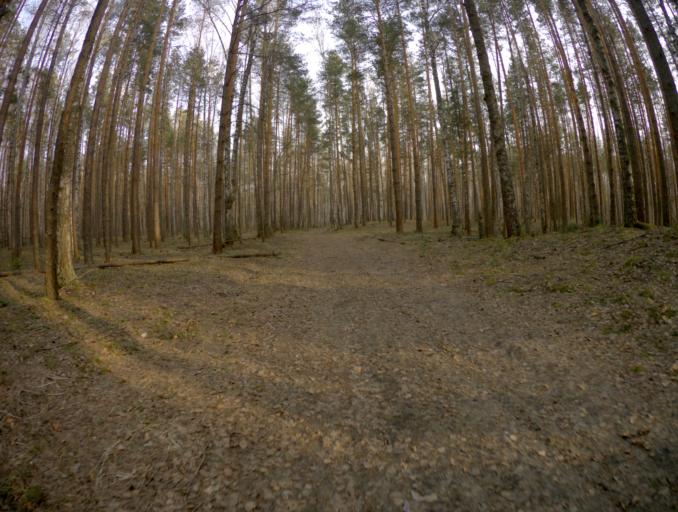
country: RU
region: Vladimir
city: Kommunar
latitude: 56.0772
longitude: 40.4392
